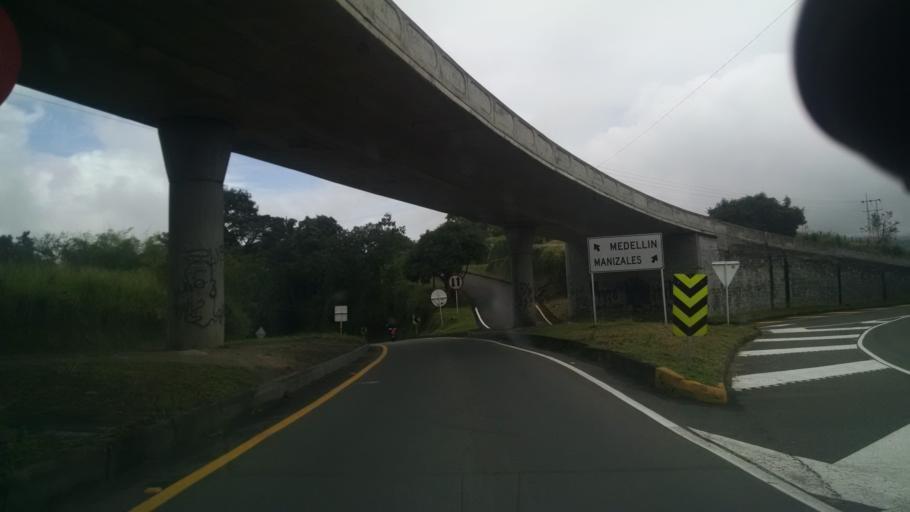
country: CO
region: Caldas
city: Palestina
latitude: 5.0181
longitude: -75.5931
